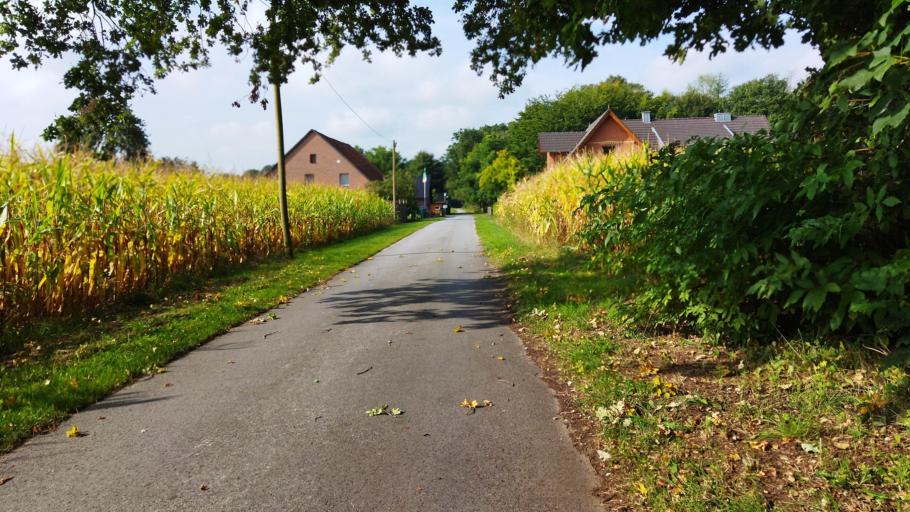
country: DE
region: Lower Saxony
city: Bad Laer
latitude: 52.0597
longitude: 8.1027
